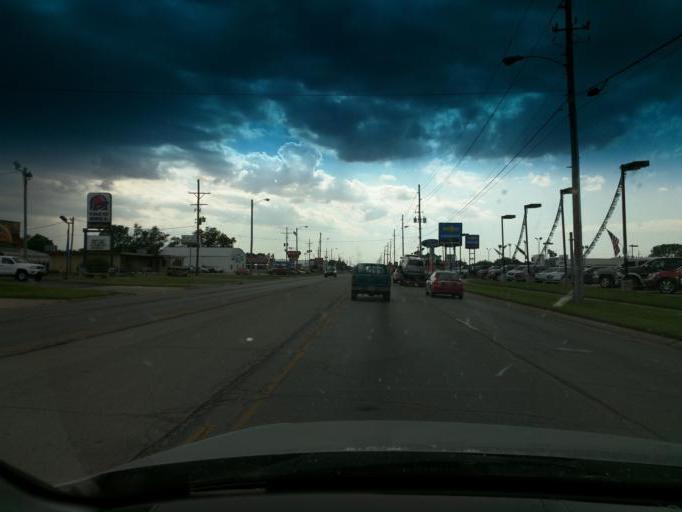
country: US
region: Kansas
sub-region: Reno County
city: Hutchinson
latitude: 38.0866
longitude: -97.9064
